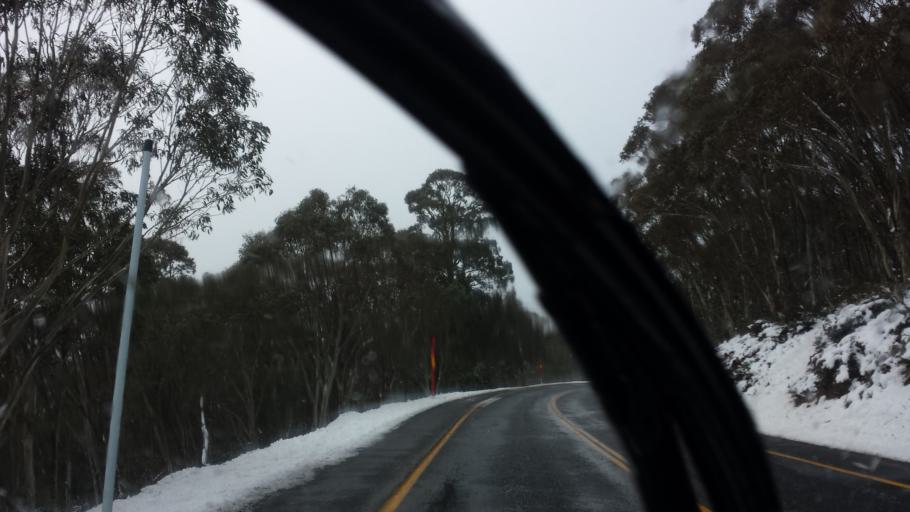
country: AU
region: Victoria
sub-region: Alpine
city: Mount Beauty
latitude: -37.0231
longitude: 147.2667
